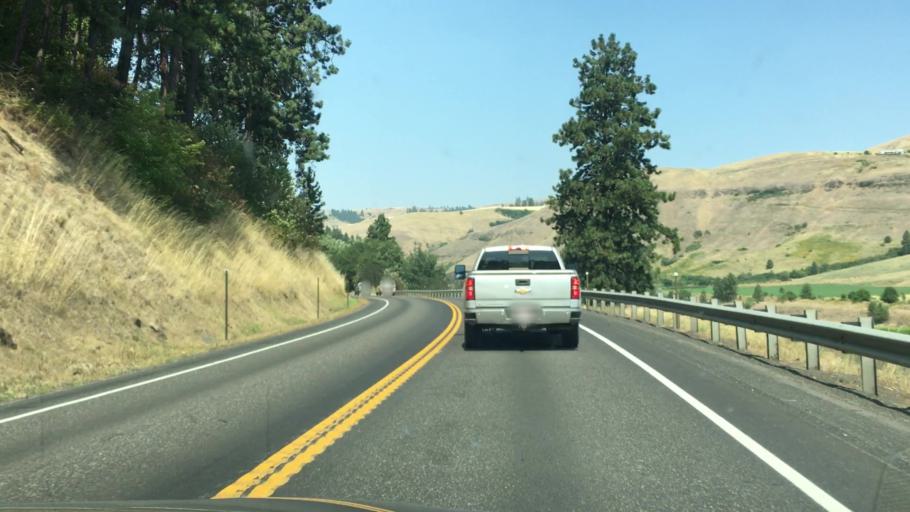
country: US
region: Idaho
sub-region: Clearwater County
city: Orofino
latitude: 46.5012
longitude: -116.5019
